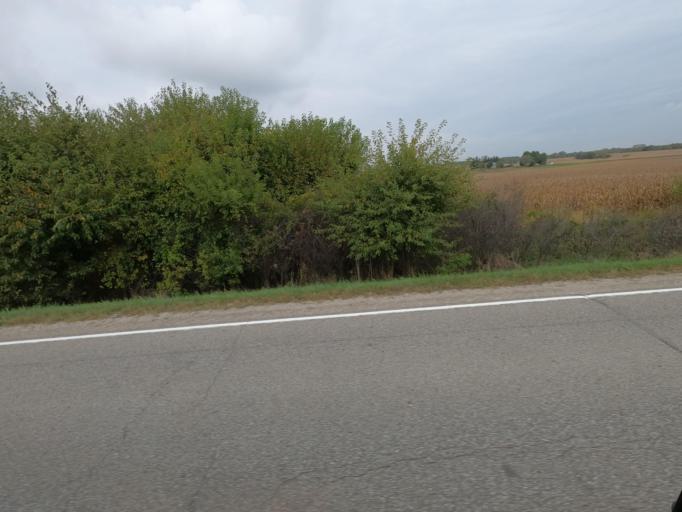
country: US
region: Iowa
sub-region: Wapello County
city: Ottumwa
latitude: 40.9016
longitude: -92.1960
